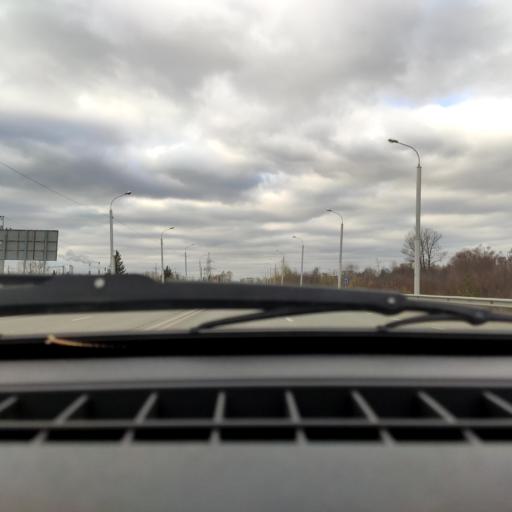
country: RU
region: Bashkortostan
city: Ufa
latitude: 54.8081
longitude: 56.1609
